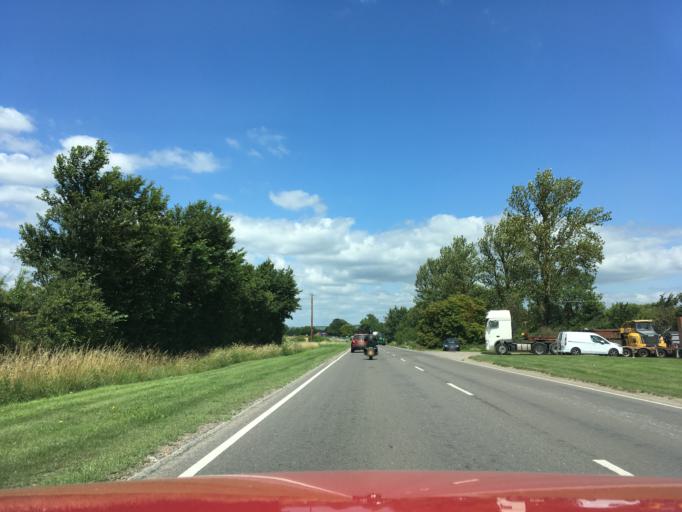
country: GB
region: England
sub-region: Buckinghamshire
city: Stone
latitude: 51.8363
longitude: -0.8726
